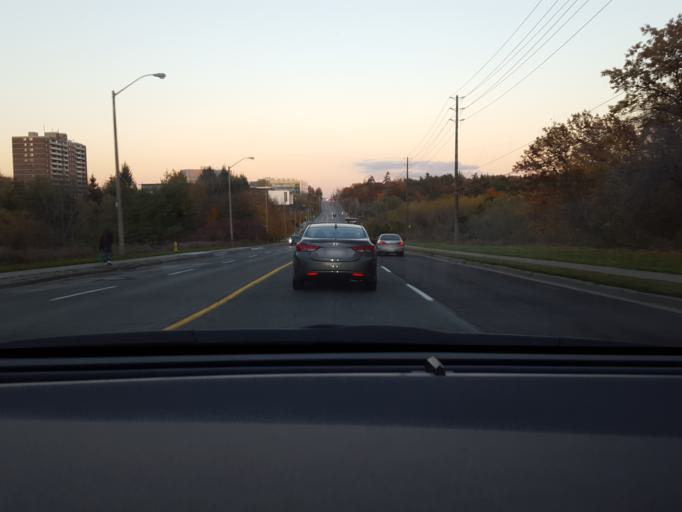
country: CA
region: Ontario
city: Scarborough
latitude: 43.7842
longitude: -79.1982
